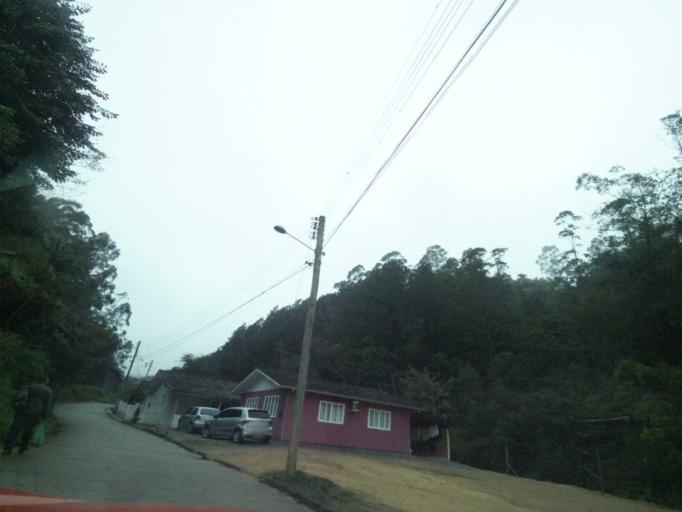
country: BR
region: Santa Catarina
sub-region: Anitapolis
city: Anitapolis
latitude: -27.9057
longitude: -49.1267
